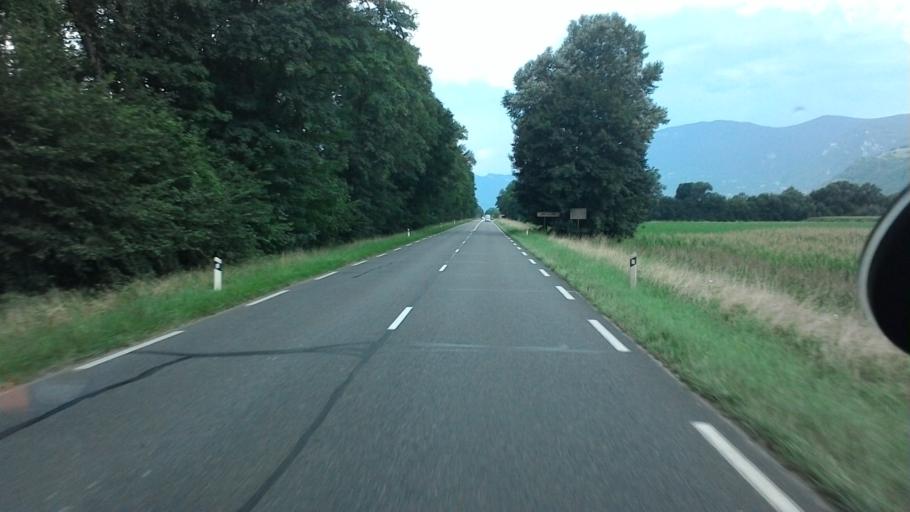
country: FR
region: Rhone-Alpes
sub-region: Departement de la Savoie
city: Aiton
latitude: 45.5723
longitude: 6.2320
